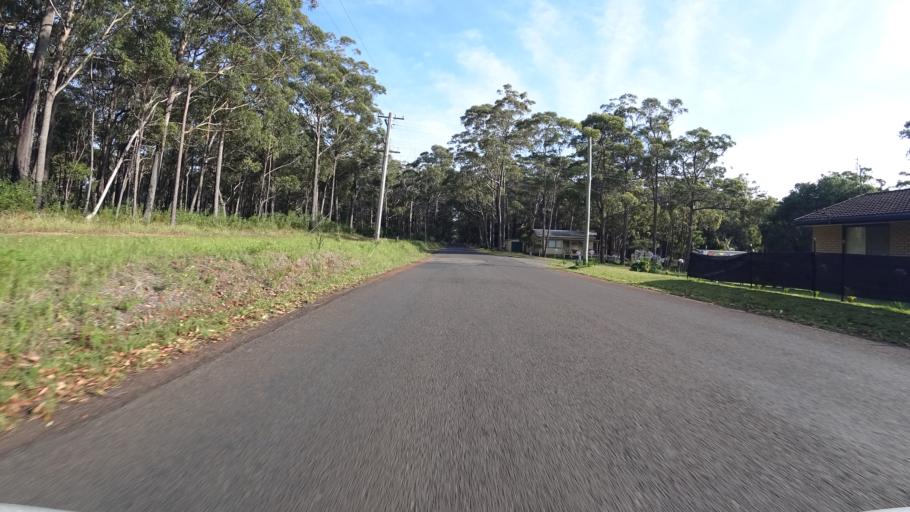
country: AU
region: New South Wales
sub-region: Shoalhaven Shire
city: Milton
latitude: -35.2576
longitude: 150.5055
